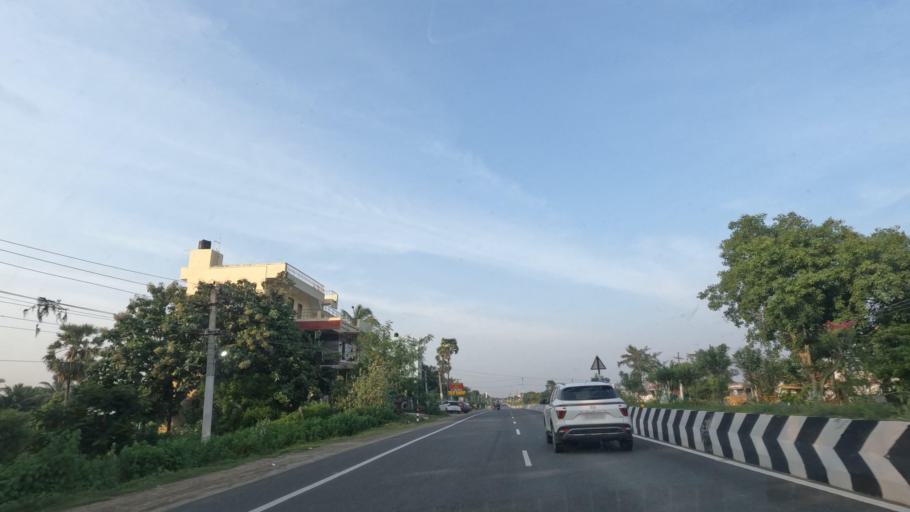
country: IN
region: Tamil Nadu
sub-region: Kancheepuram
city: Mamallapuram
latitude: 12.6936
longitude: 80.2190
